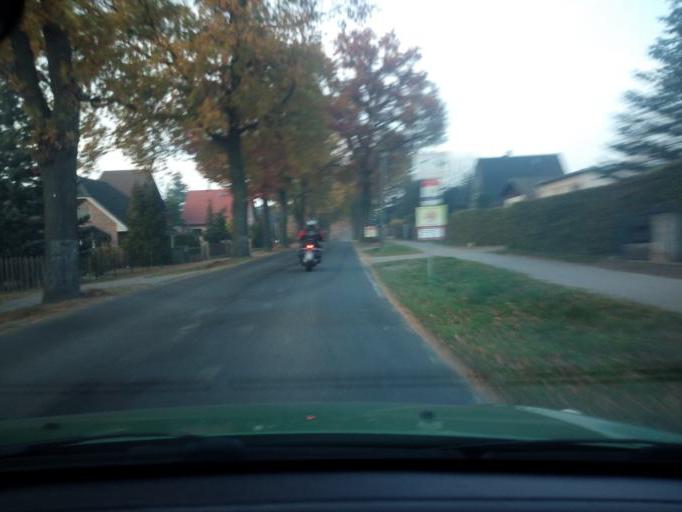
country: DE
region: Brandenburg
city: Neuenhagen
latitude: 52.5075
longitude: 13.7065
